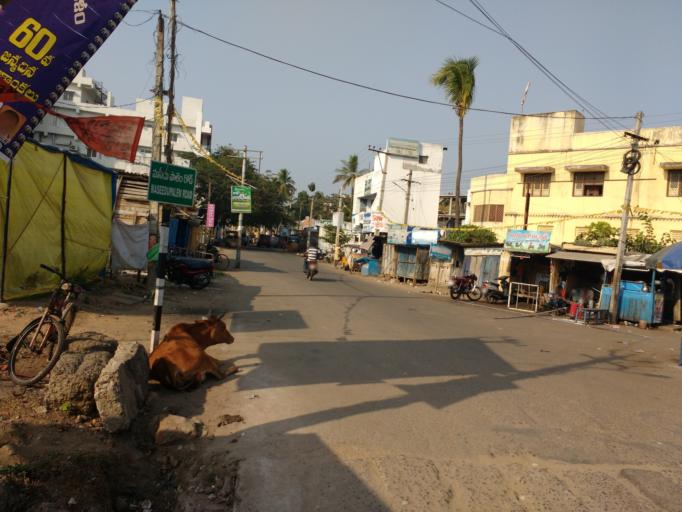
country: IN
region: Andhra Pradesh
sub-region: Srikakulam
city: Srikakulam
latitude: 18.2949
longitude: 83.9002
